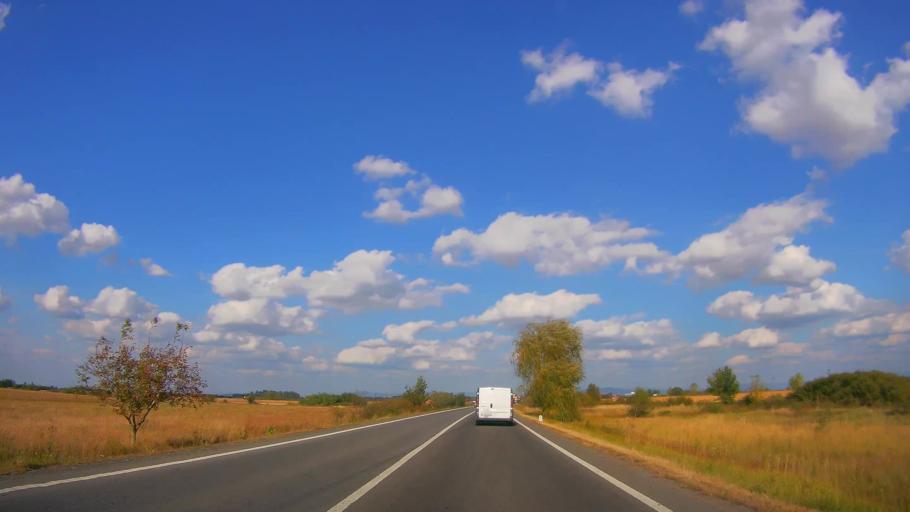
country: RO
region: Satu Mare
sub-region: Comuna Agris
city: Agris
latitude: 47.8608
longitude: 22.9868
